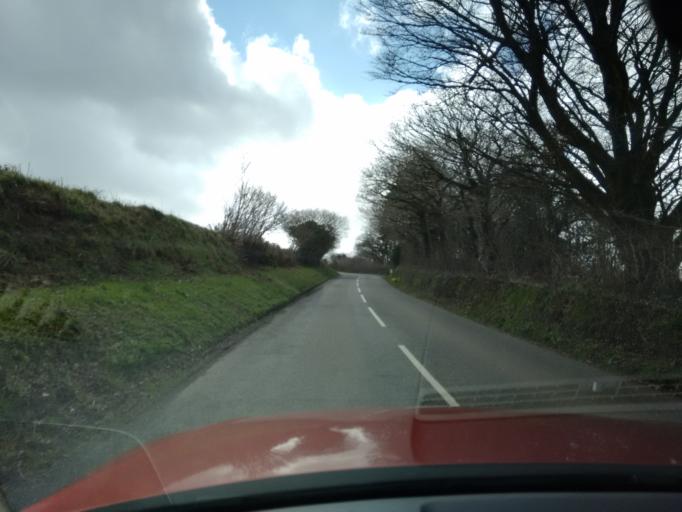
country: GB
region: England
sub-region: Cornwall
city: Liskeard
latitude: 50.4883
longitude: -4.5033
